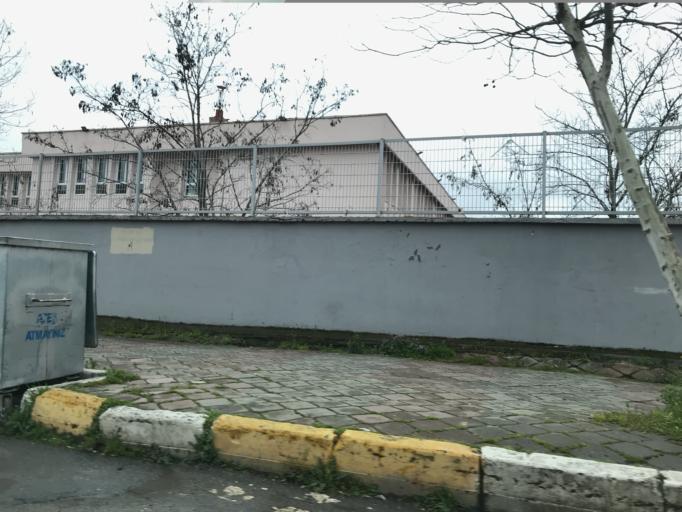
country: TR
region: Istanbul
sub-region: Atasehir
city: Atasehir
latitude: 40.9867
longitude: 29.0957
